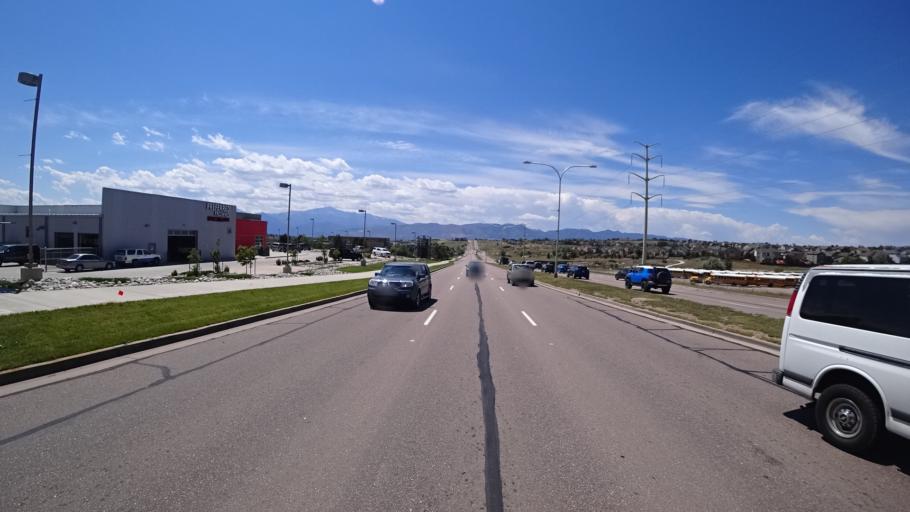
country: US
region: Colorado
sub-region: El Paso County
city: Black Forest
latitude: 38.9402
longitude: -104.7311
